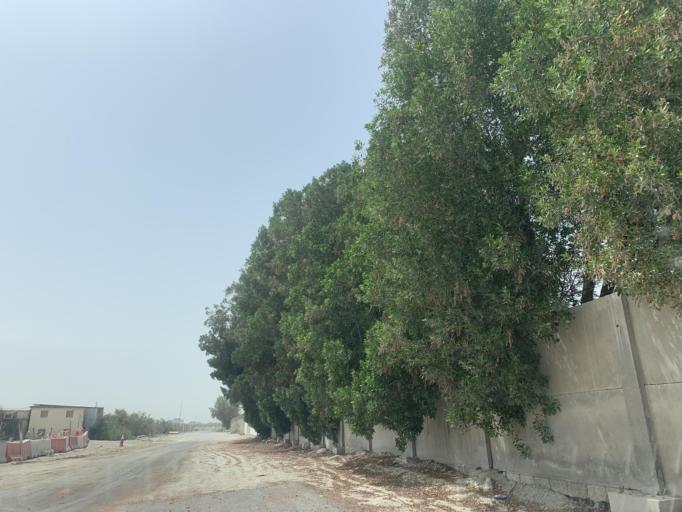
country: BH
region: Northern
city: Madinat `Isa
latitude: 26.1923
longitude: 50.5293
